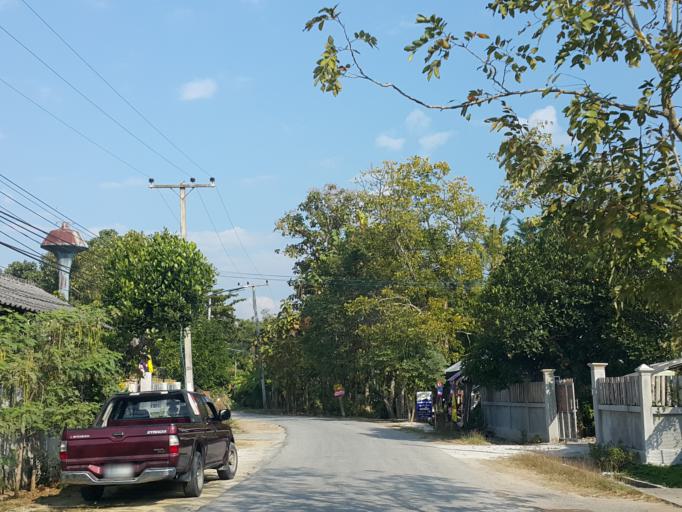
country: TH
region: Chiang Mai
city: San Sai
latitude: 18.8408
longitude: 99.1013
